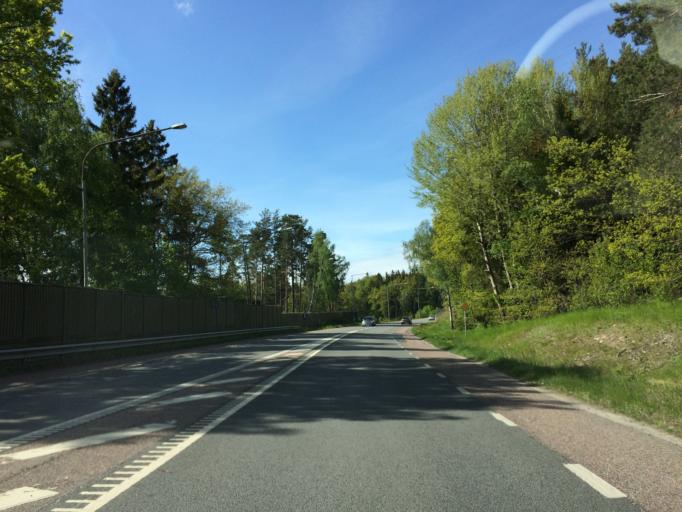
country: SE
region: Stockholm
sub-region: Norrtalje Kommun
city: Bergshamra
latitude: 59.4195
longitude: 18.0061
